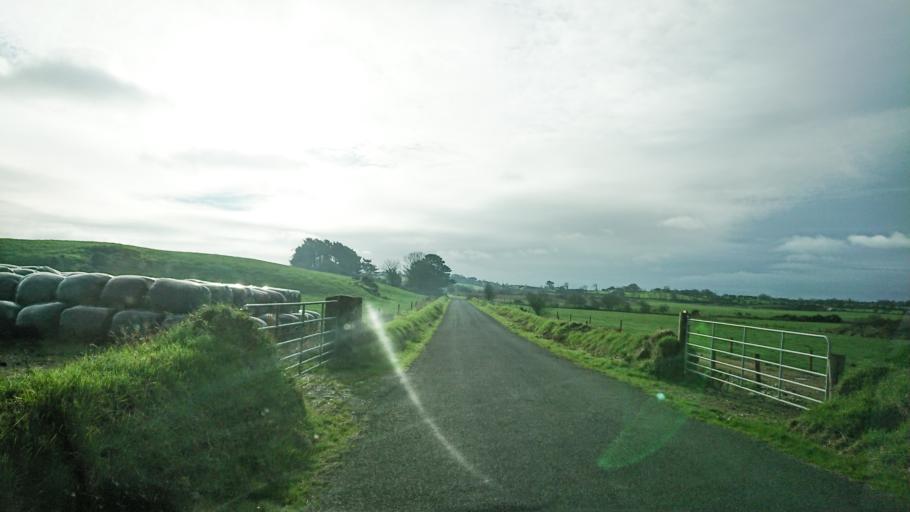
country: IE
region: Munster
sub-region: Waterford
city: Tra Mhor
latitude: 52.1639
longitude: -7.1874
